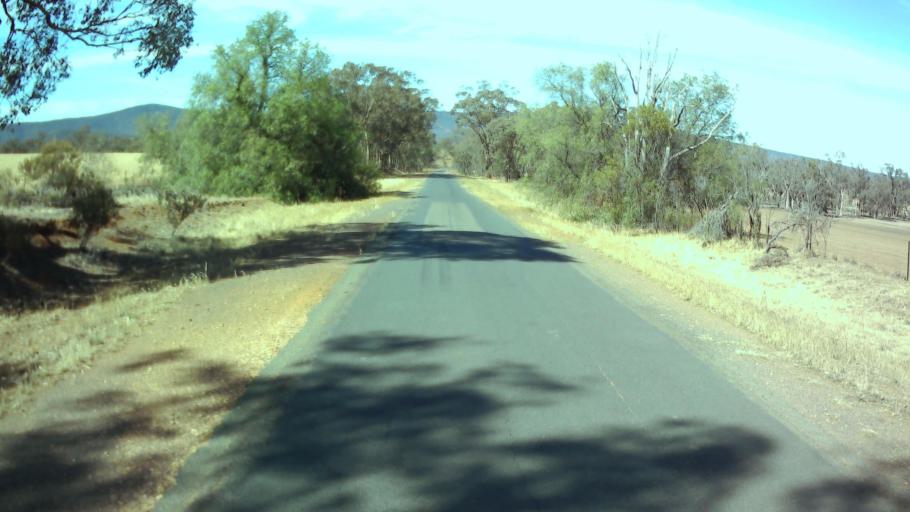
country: AU
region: New South Wales
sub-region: Weddin
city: Grenfell
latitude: -33.9358
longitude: 148.0820
